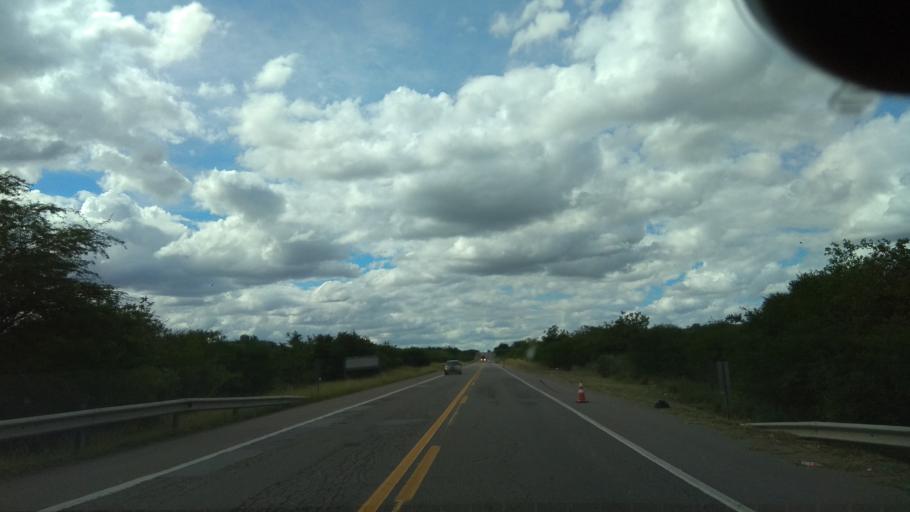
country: BR
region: Bahia
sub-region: Santa Ines
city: Santa Ines
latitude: -12.9810
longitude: -39.9407
